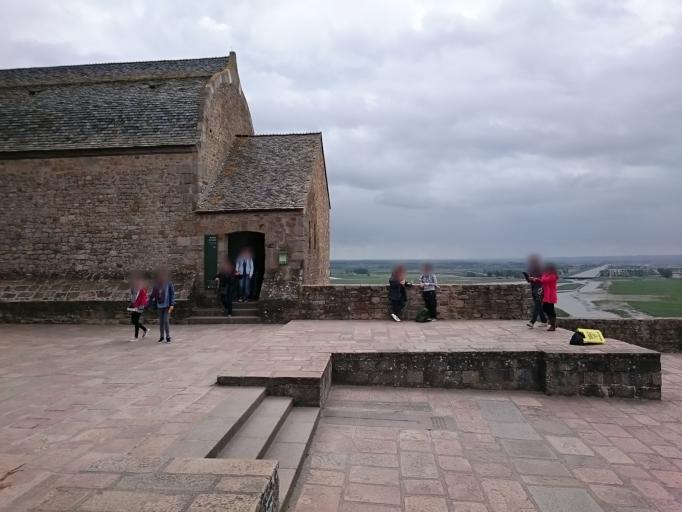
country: FR
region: Lower Normandy
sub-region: Departement de la Manche
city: Pontorson
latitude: 48.6360
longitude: -1.5120
